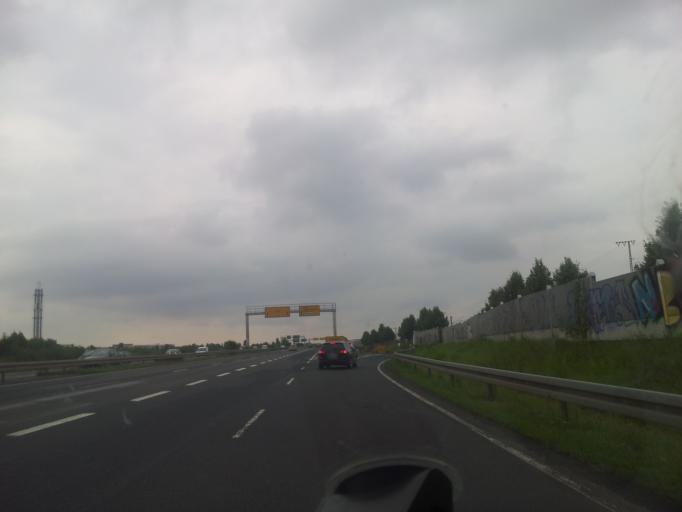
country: DE
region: Saxony
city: Rackwitz
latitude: 51.4019
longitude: 12.3881
